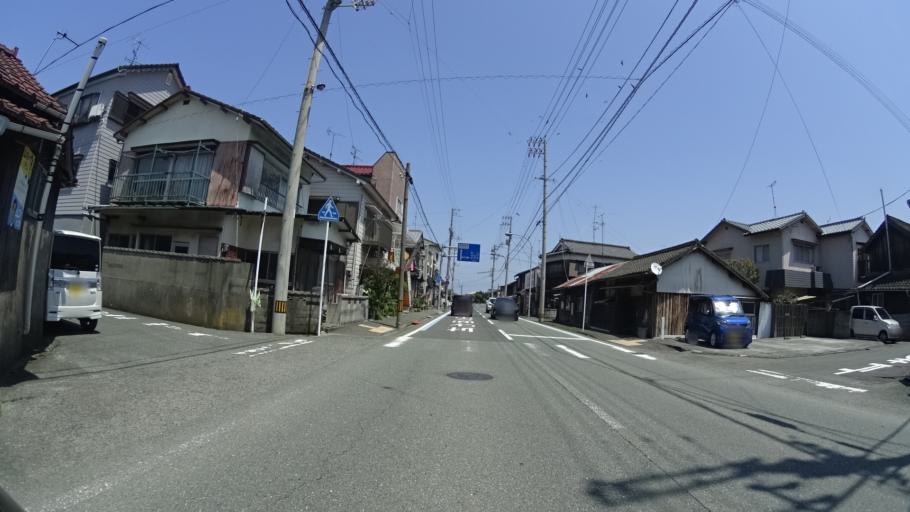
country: JP
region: Ehime
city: Ozu
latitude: 33.6153
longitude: 132.4806
